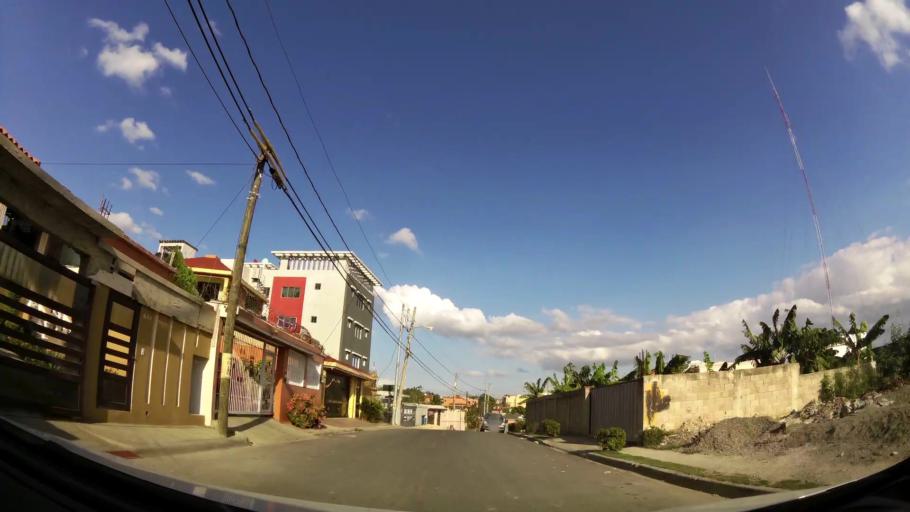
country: DO
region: Nacional
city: Ensanche Luperon
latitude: 18.5483
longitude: -69.9076
